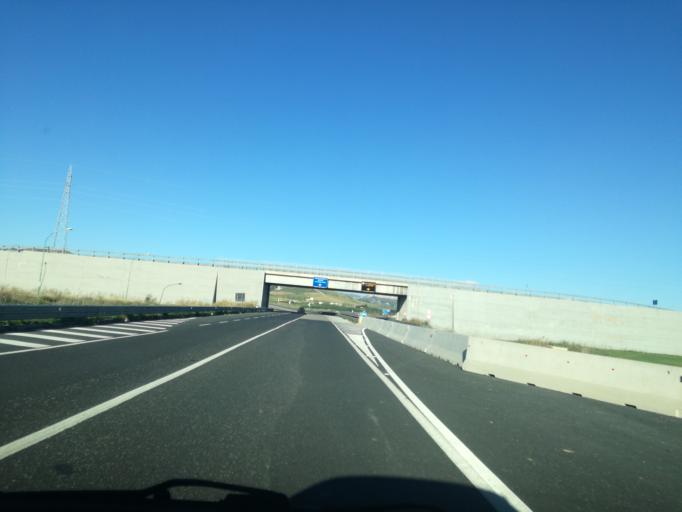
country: IT
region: Sicily
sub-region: Provincia di Caltanissetta
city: Butera
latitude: 37.1283
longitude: 14.1210
